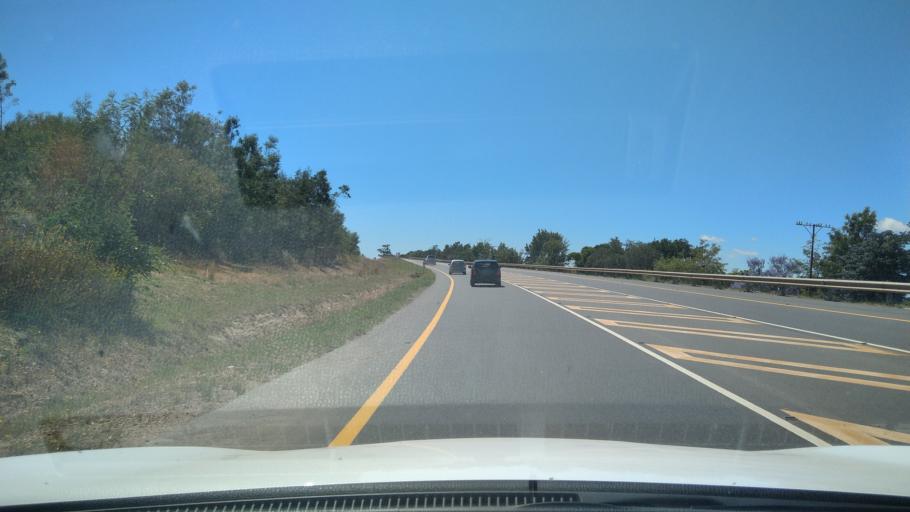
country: ZA
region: Western Cape
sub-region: Overberg District Municipality
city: Caledon
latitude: -34.2259
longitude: 19.4175
